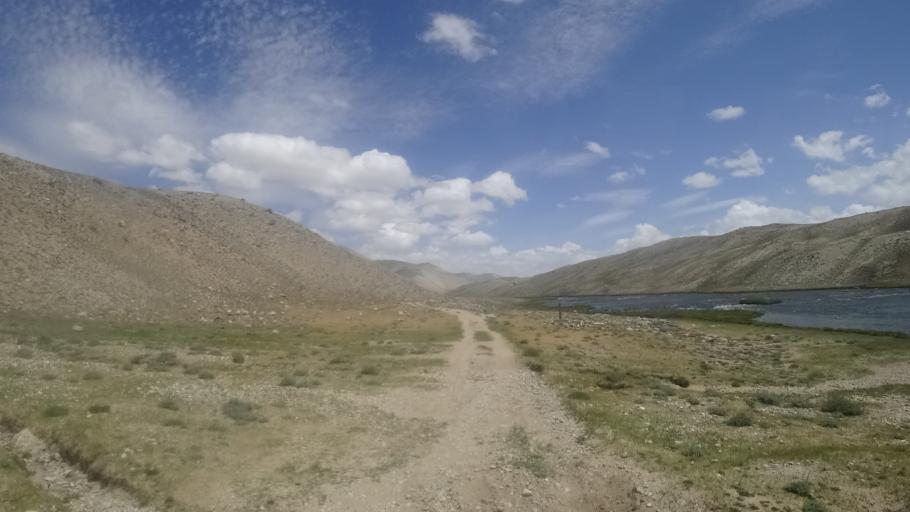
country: TJ
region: Gorno-Badakhshan
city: Murghob
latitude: 37.4715
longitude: 73.4372
